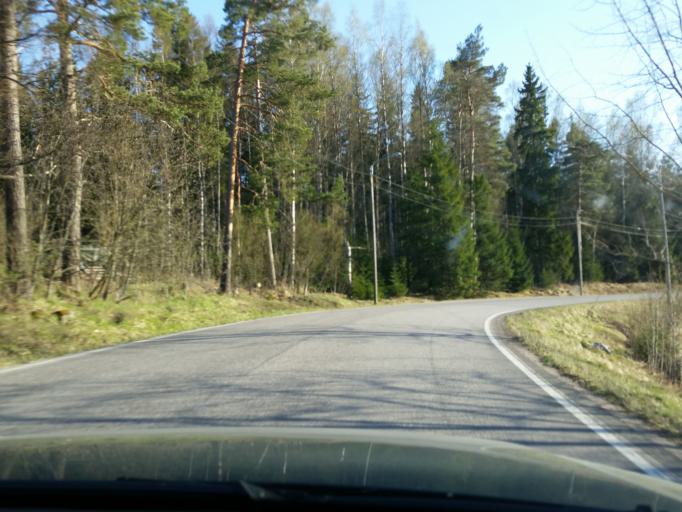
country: FI
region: Uusimaa
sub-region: Helsinki
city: Espoo
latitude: 60.1096
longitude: 24.5694
